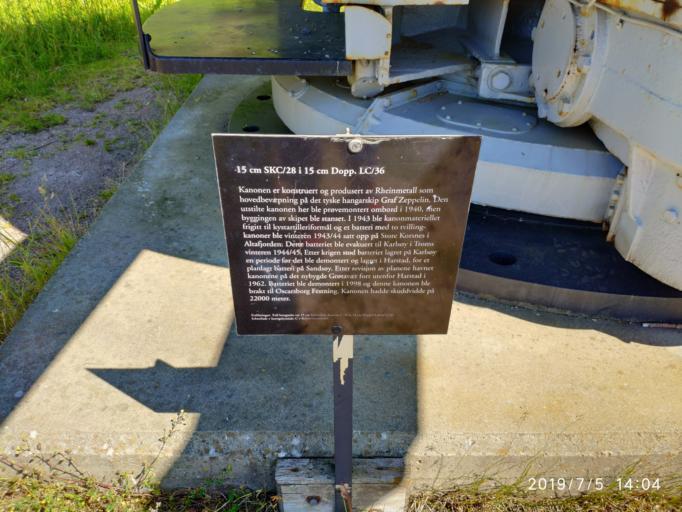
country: NO
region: Akershus
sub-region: Frogn
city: Drobak
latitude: 59.6736
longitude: 10.6051
